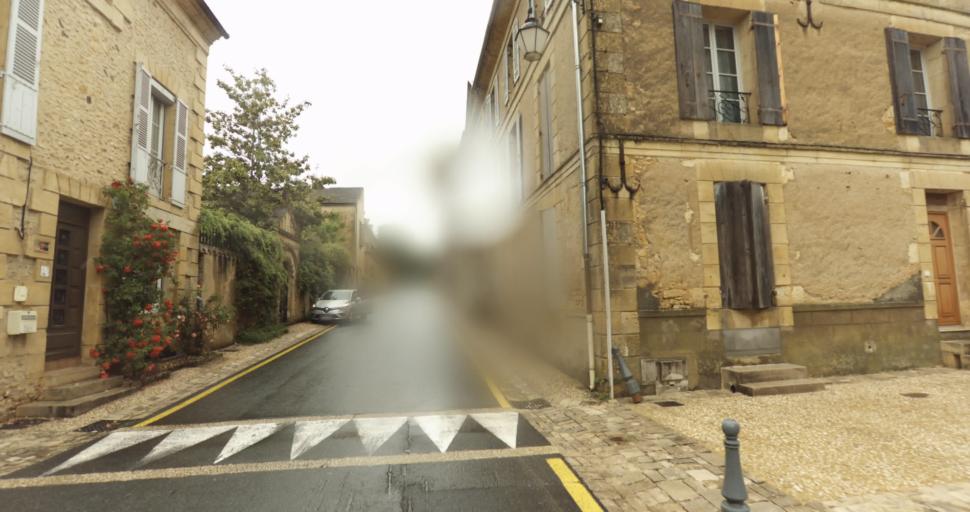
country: FR
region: Aquitaine
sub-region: Departement de la Dordogne
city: Beaumont-du-Perigord
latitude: 44.8119
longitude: 0.8741
